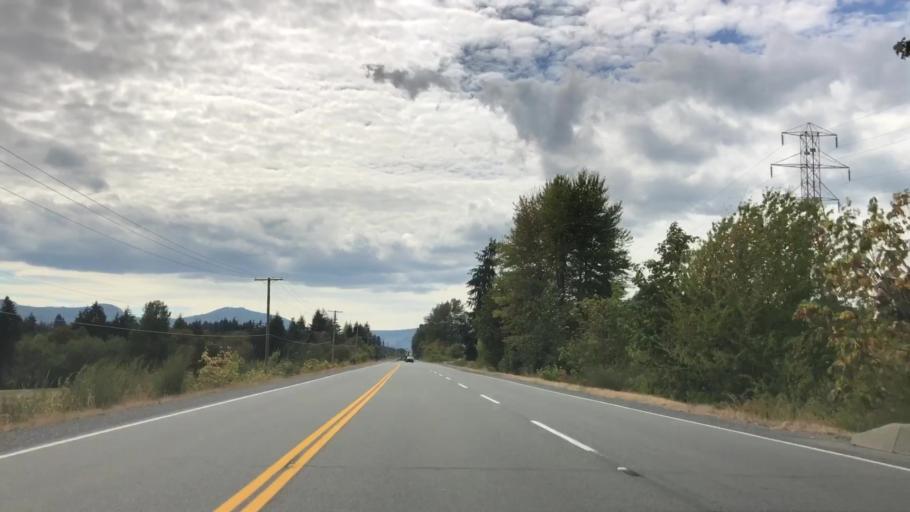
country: CA
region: British Columbia
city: Duncan
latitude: 48.8121
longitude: -123.7487
